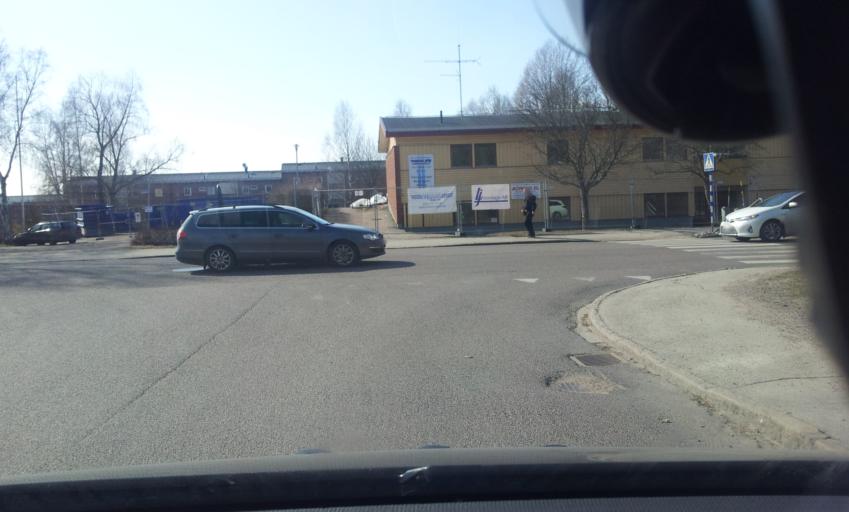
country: SE
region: Gaevleborg
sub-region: Ljusdals Kommun
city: Ljusdal
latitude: 61.8264
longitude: 16.1084
